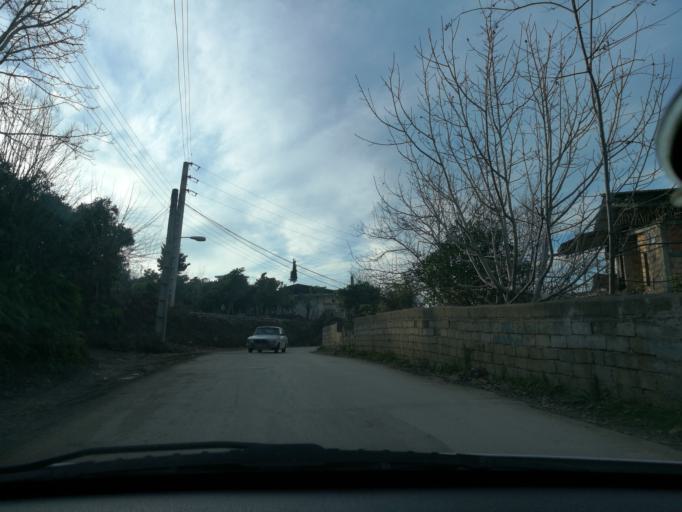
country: IR
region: Mazandaran
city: Chalus
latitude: 36.6430
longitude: 51.4367
